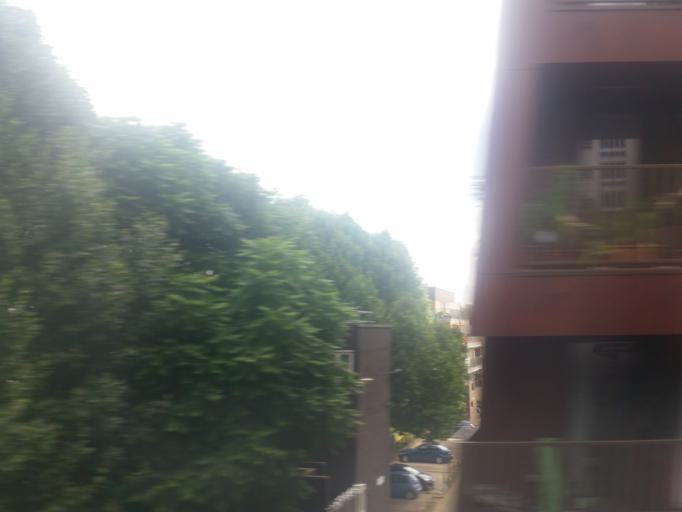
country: GB
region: England
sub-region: Greater London
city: Kennington
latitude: 51.4956
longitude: -0.0983
